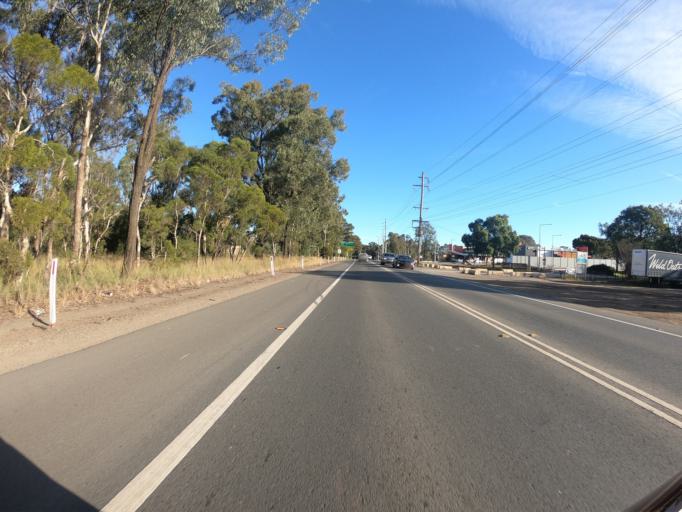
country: AU
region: New South Wales
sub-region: Hawkesbury
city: South Windsor
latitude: -33.6375
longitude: 150.7860
